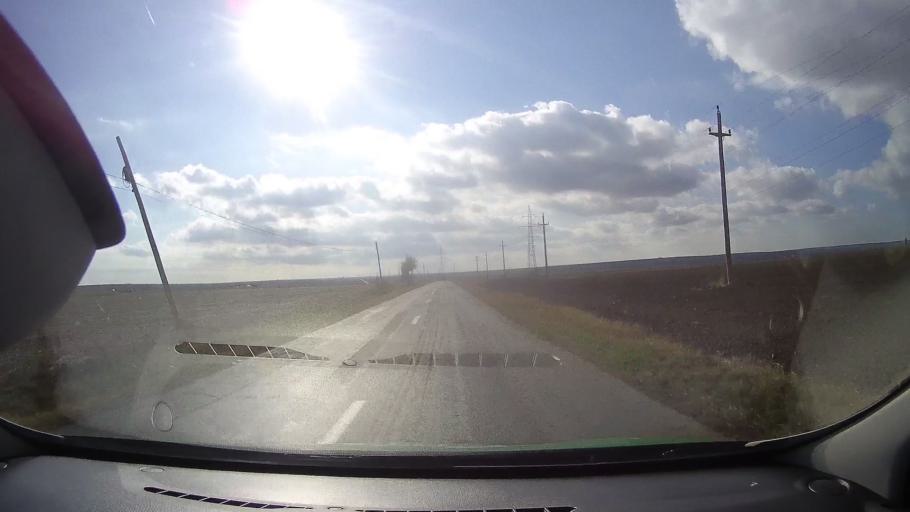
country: RO
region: Constanta
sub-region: Comuna Istria
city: Nuntasi
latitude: 44.5355
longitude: 28.6865
